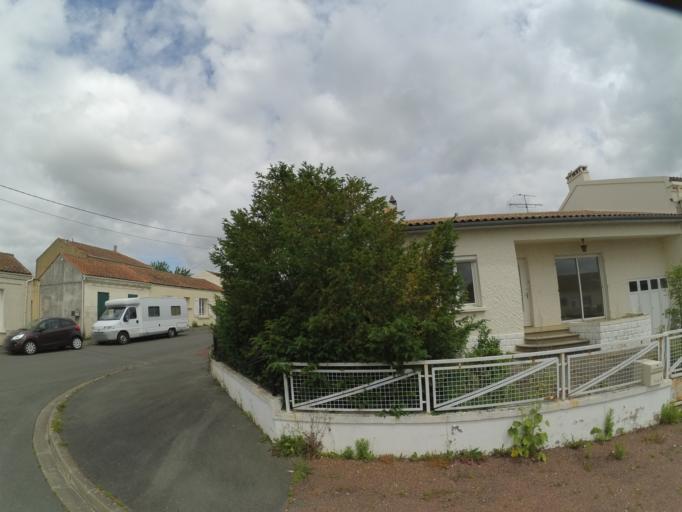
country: FR
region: Poitou-Charentes
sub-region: Departement de la Charente-Maritime
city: Rochefort
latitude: 45.9508
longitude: -0.9683
